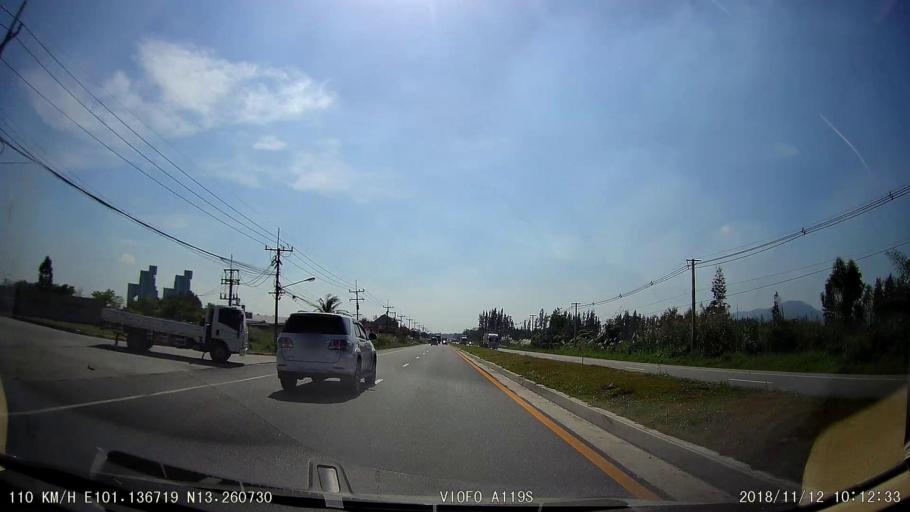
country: TH
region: Chon Buri
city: Ban Bueng
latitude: 13.2603
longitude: 101.1370
